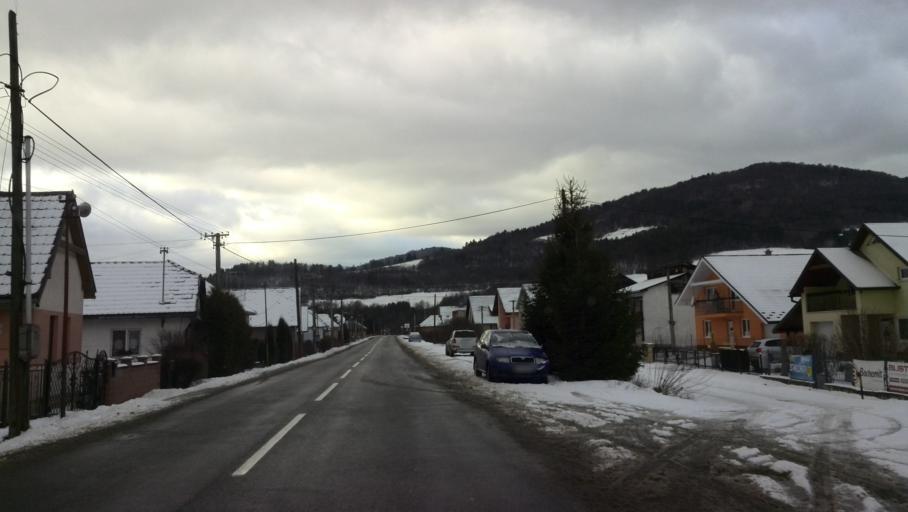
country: SK
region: Kosicky
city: Gelnica
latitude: 48.8736
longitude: 20.9884
